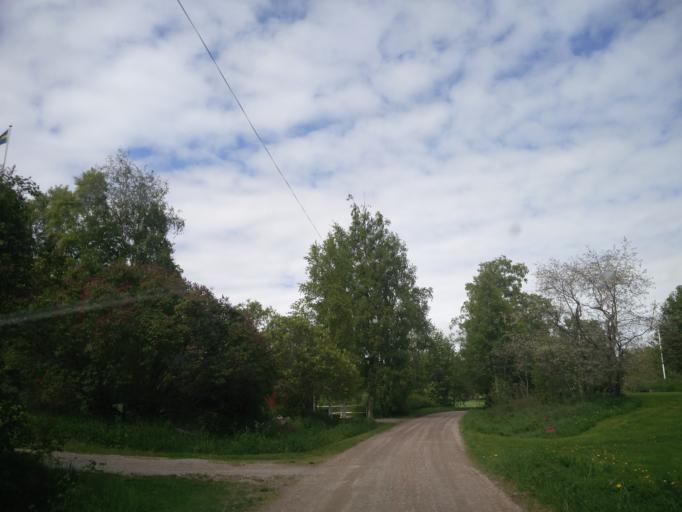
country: SE
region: Vaesternorrland
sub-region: Sundsvalls Kommun
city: Njurundabommen
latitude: 62.2250
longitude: 17.3573
